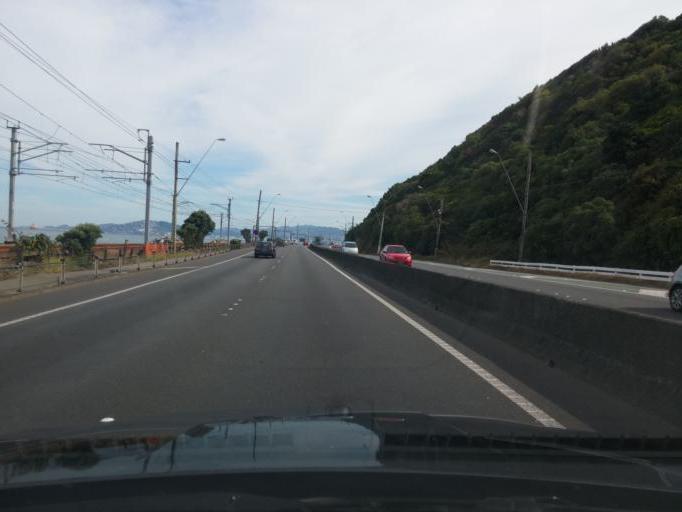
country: NZ
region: Wellington
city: Petone
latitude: -41.2329
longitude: 174.8368
